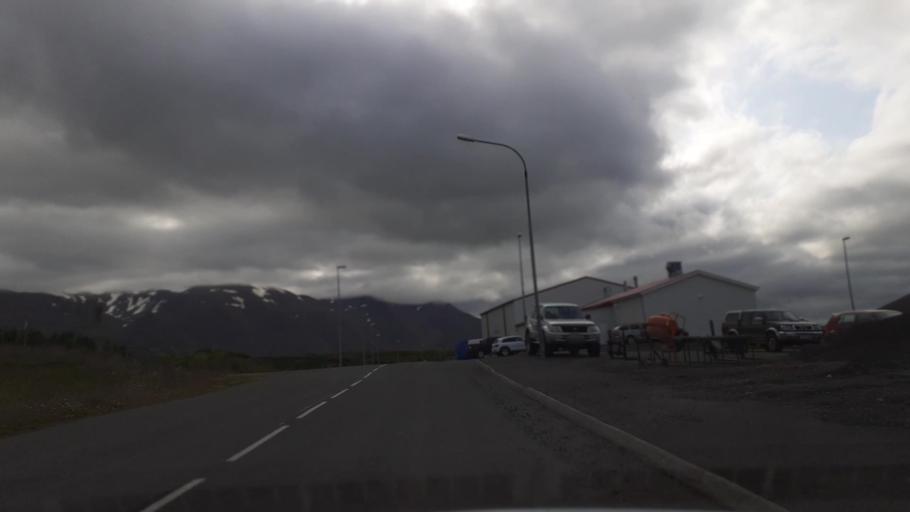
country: IS
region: Northeast
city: Akureyri
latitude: 65.9526
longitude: -18.1788
